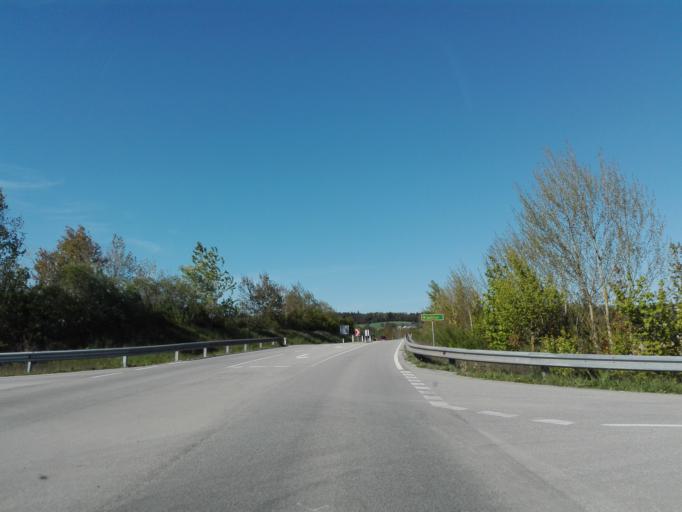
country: AT
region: Upper Austria
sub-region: Politischer Bezirk Perg
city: Perg
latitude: 48.2399
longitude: 14.6463
